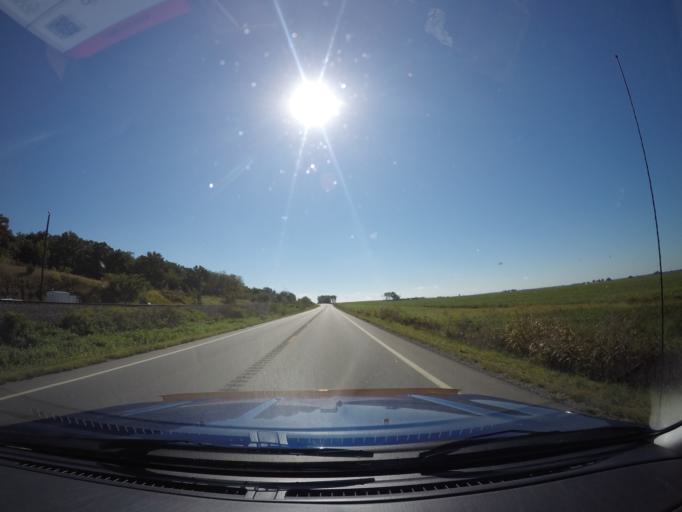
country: US
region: Kansas
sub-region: Pottawatomie County
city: Saint Marys
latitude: 39.1772
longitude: -96.0305
